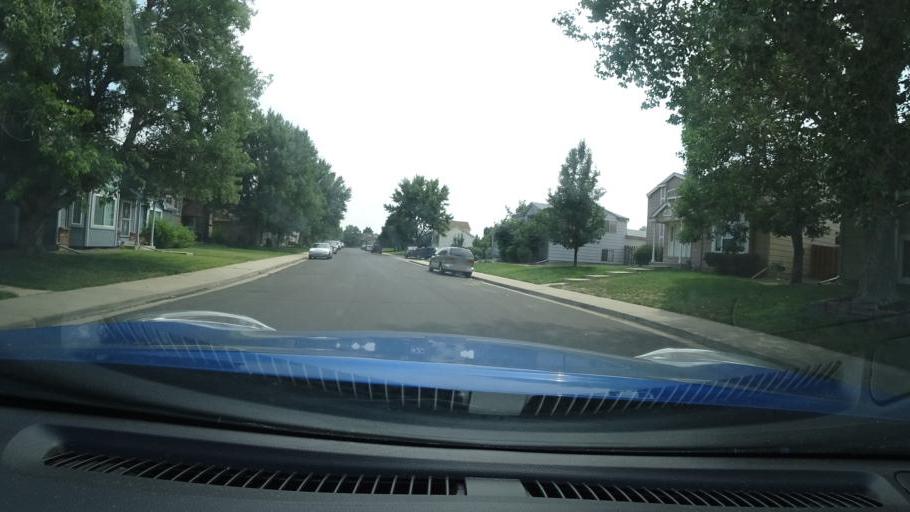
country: US
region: Colorado
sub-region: Adams County
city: Aurora
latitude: 39.7772
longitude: -104.7416
